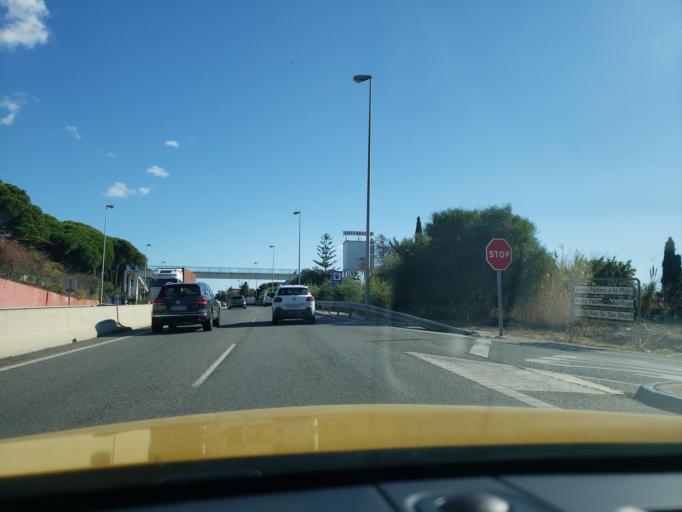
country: ES
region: Andalusia
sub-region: Provincia de Malaga
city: Ojen
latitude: 36.5022
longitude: -4.8057
